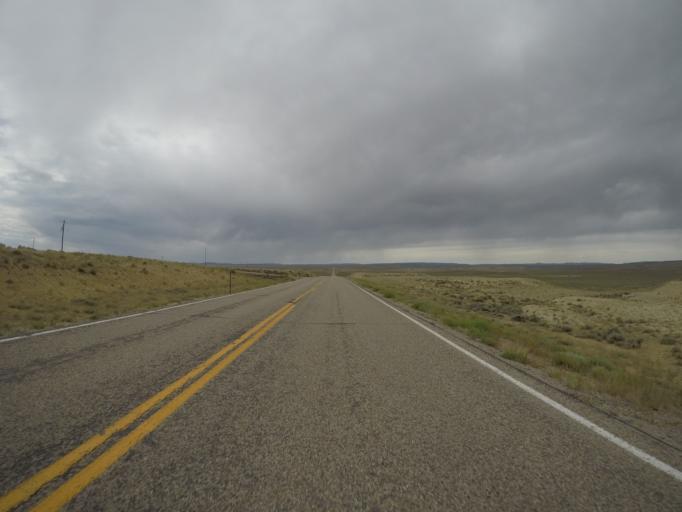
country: US
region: Wyoming
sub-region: Lincoln County
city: Kemmerer
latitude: 41.9632
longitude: -110.1311
